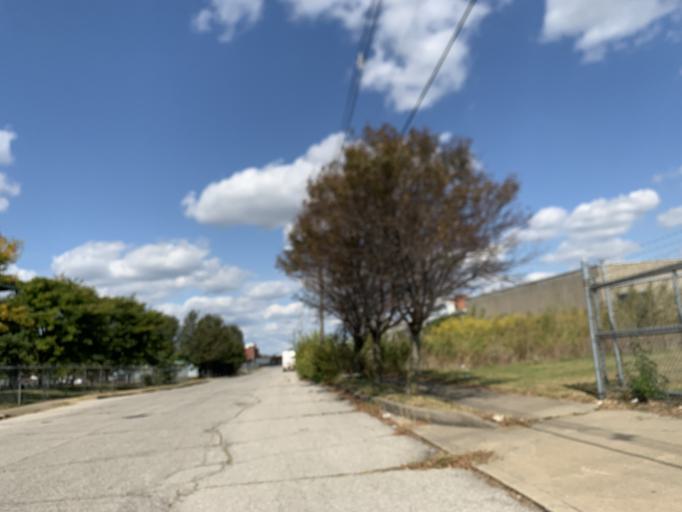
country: US
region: Kentucky
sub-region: Jefferson County
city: Louisville
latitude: 38.2426
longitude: -85.7706
